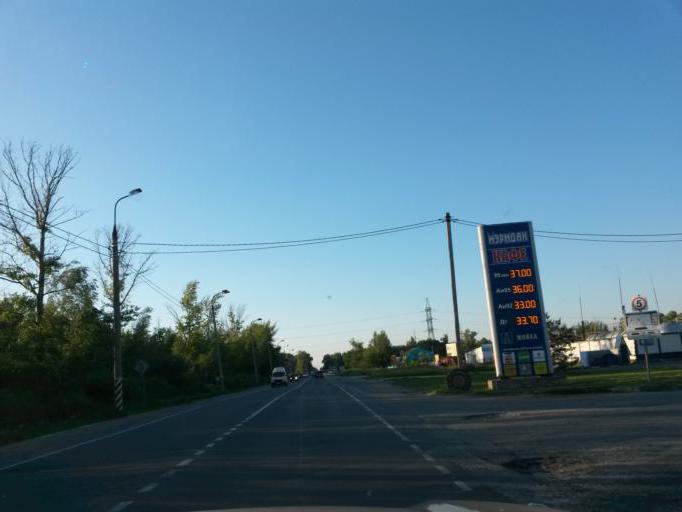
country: RU
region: Moskovskaya
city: Serpukhov
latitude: 54.9505
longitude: 37.4091
